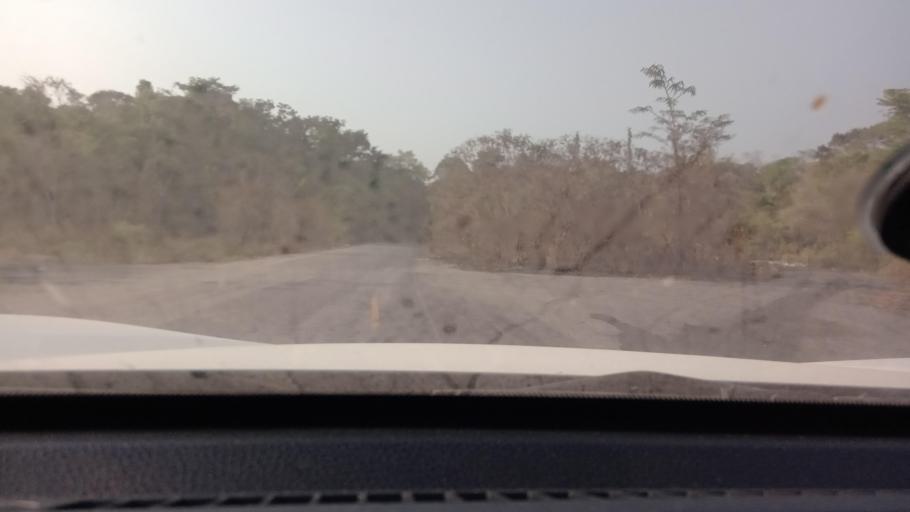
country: MX
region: Tabasco
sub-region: Huimanguillo
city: Francisco Rueda
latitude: 17.6711
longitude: -93.8670
